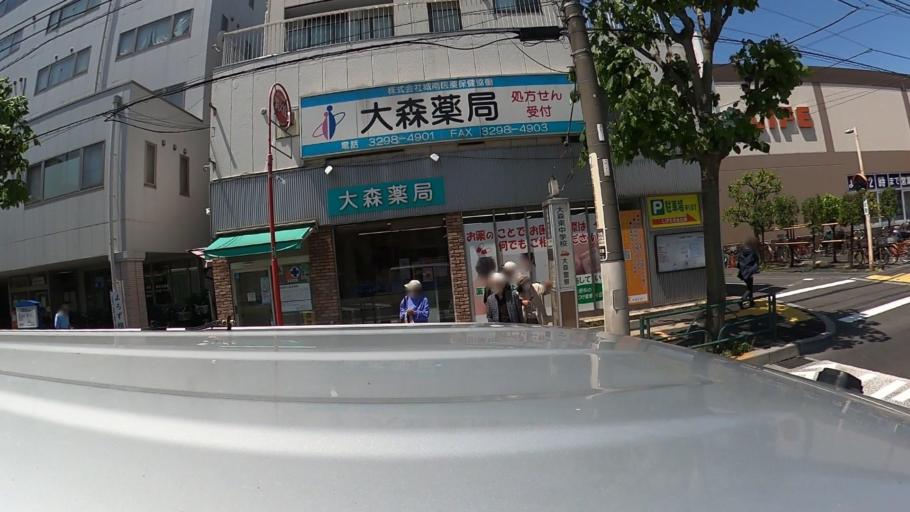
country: JP
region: Kanagawa
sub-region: Kawasaki-shi
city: Kawasaki
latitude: 35.5689
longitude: 139.7353
